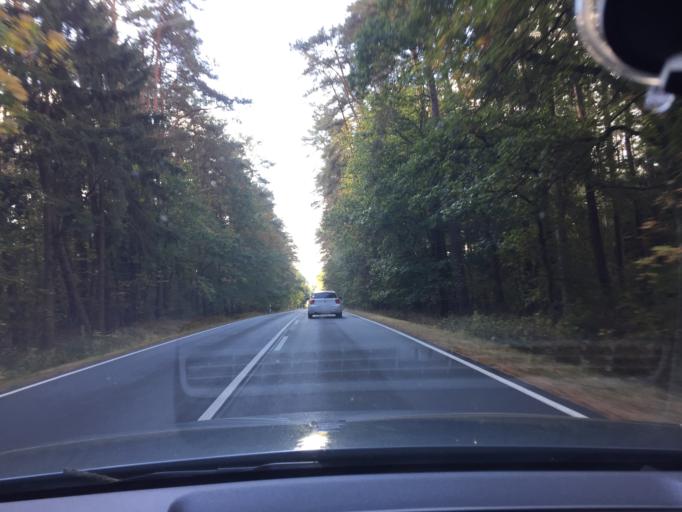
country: DE
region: Mecklenburg-Vorpommern
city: Krakow am See
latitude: 53.6259
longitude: 12.2537
